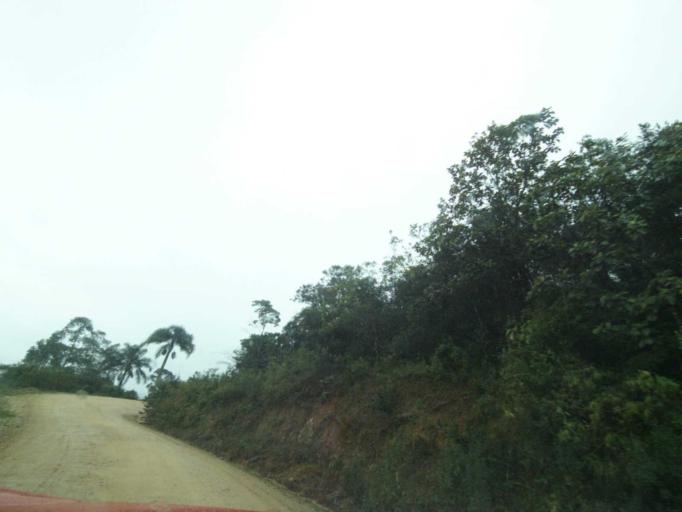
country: BR
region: Santa Catarina
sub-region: Anitapolis
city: Anitapolis
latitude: -27.9239
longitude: -49.1790
